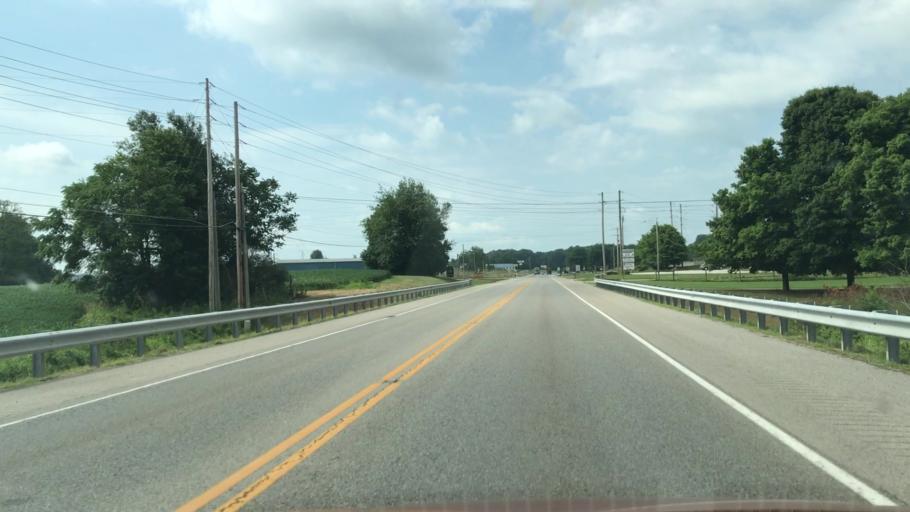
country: US
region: Kentucky
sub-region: Barren County
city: Cave City
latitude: 37.1225
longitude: -85.9619
